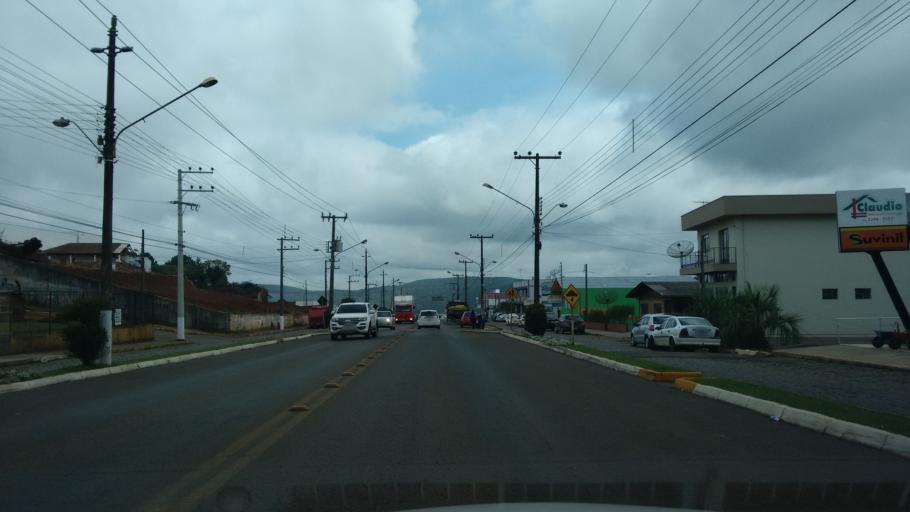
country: BR
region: Santa Catarina
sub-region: Videira
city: Videira
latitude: -27.0305
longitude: -50.9165
